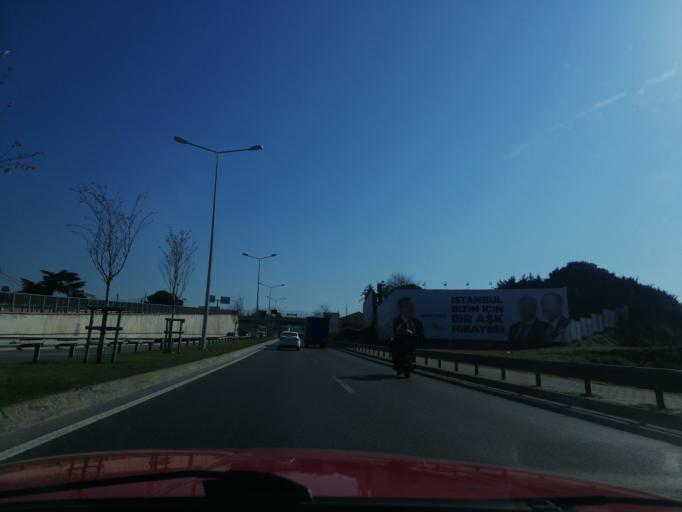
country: TR
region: Istanbul
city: Umraniye
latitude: 41.1017
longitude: 29.0973
